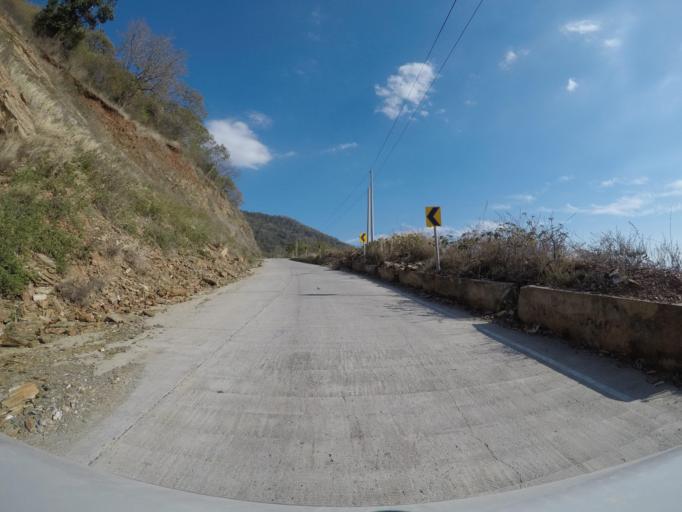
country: TL
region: Liquica
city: Maubara
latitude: -8.6707
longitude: 125.1086
